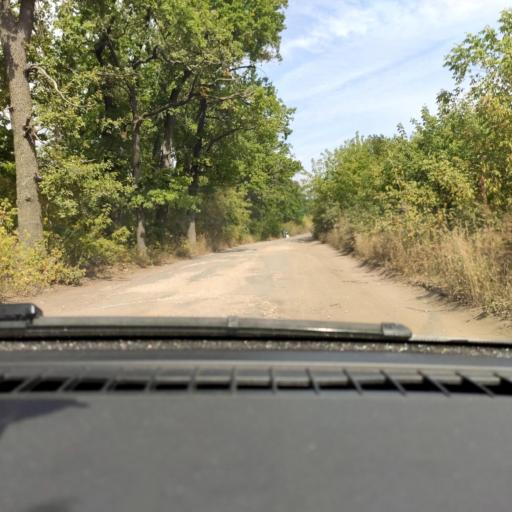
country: RU
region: Voronezj
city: Pridonskoy
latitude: 51.7447
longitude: 39.0734
